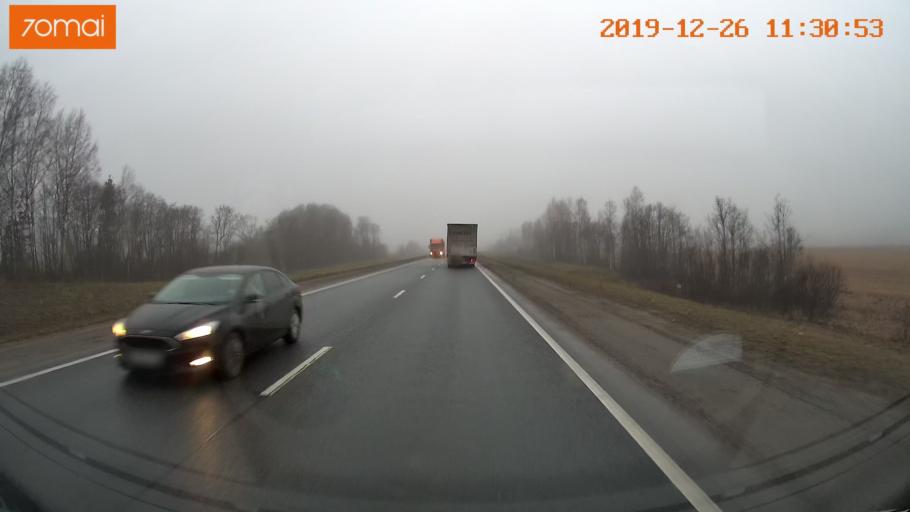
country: RU
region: Vologda
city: Chebsara
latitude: 59.1670
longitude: 38.7641
